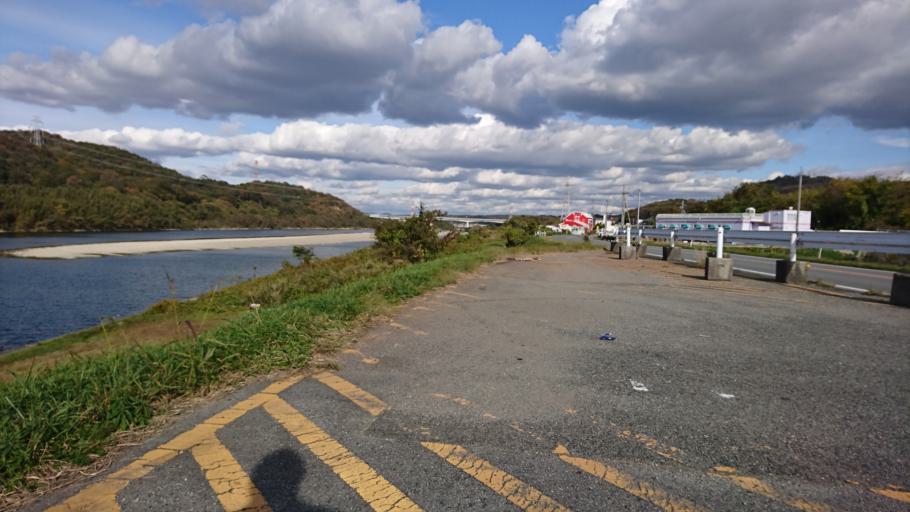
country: JP
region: Hyogo
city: Ono
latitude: 34.8036
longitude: 134.9206
